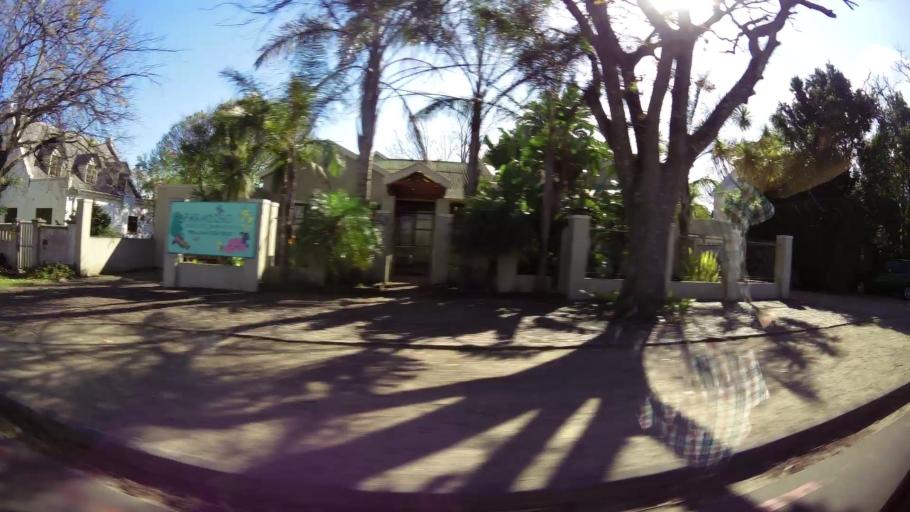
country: ZA
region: Western Cape
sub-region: Eden District Municipality
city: George
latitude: -33.9662
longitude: 22.4552
